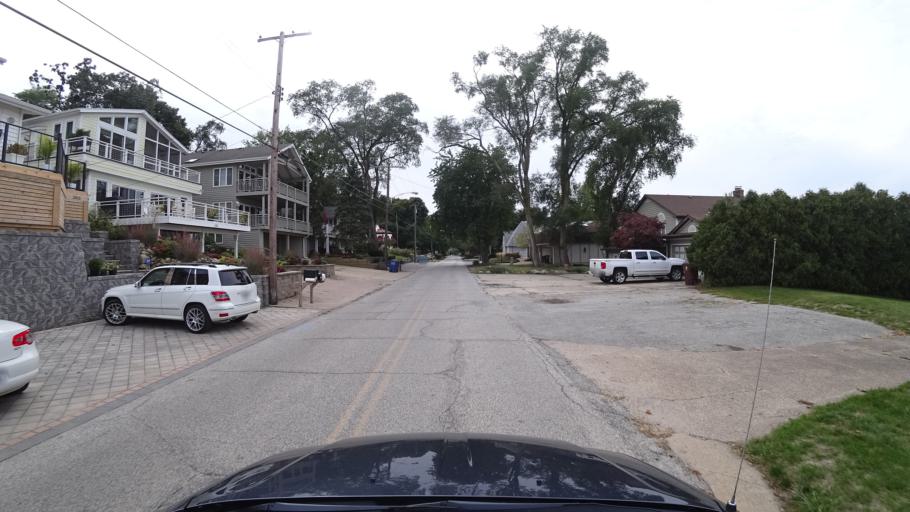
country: US
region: Indiana
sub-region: LaPorte County
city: Long Beach
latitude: 41.7429
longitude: -86.8625
